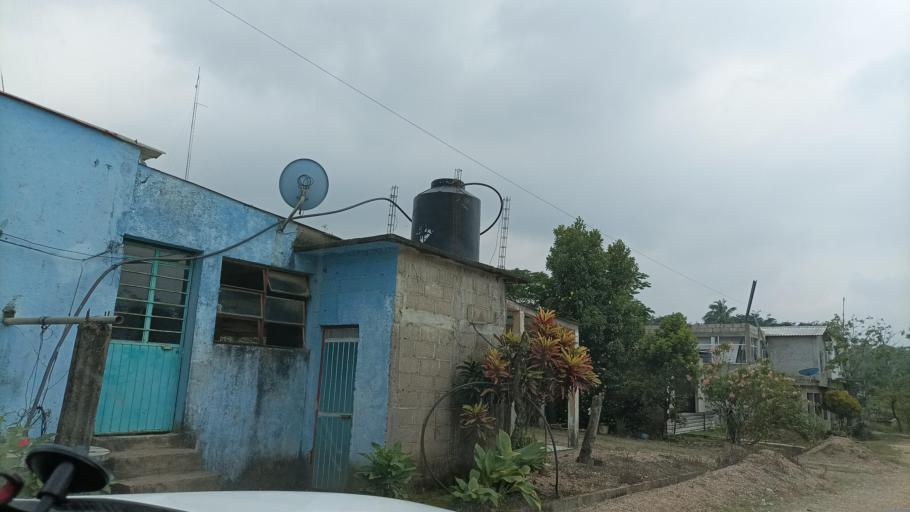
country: MX
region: Veracruz
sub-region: Moloacan
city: Cuichapa
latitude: 17.5803
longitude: -94.2303
